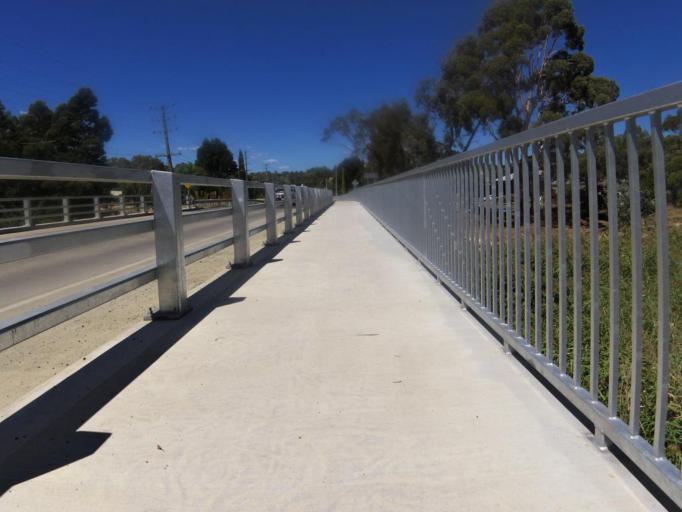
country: AU
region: Victoria
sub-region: Mount Alexander
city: Castlemaine
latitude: -37.0709
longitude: 144.2023
